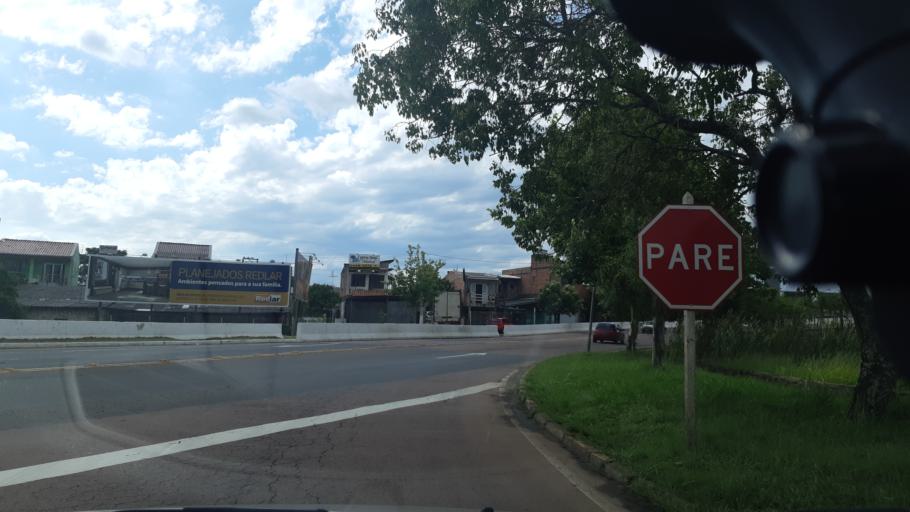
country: BR
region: Rio Grande do Sul
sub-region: Esteio
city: Esteio
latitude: -29.8454
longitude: -51.1777
